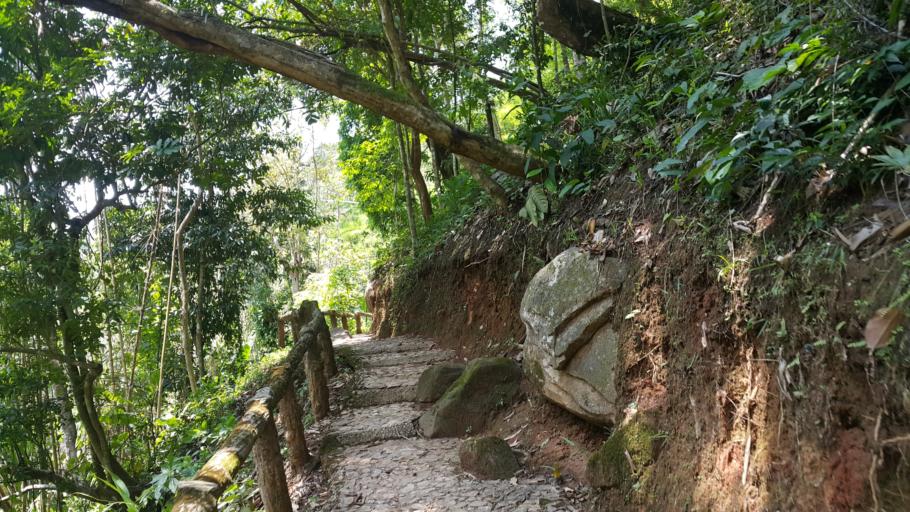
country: TH
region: Chiang Rai
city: Chiang Rai
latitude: 20.0054
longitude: 99.7160
